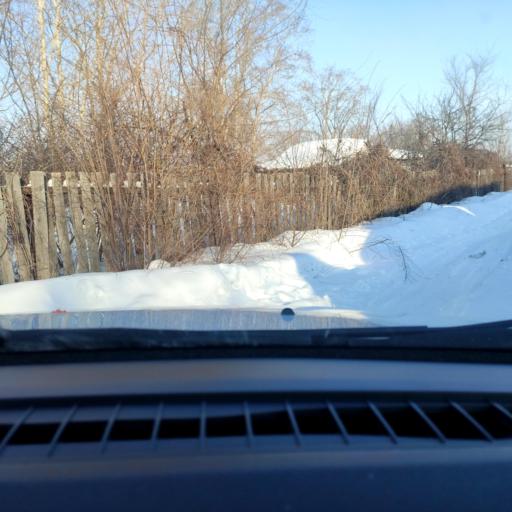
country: RU
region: Samara
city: Samara
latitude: 53.1319
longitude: 50.2546
